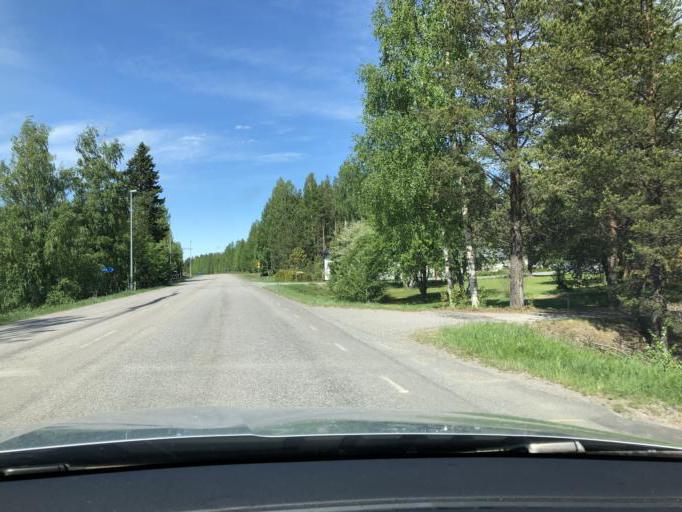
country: SE
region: Norrbotten
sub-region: Pitea Kommun
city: Bergsviken
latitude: 65.3805
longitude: 21.3399
